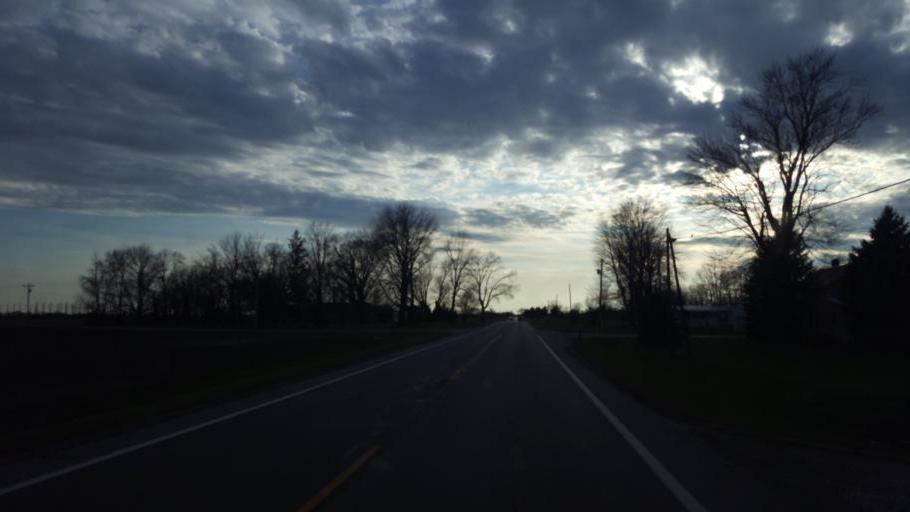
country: US
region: Ohio
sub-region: Marion County
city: Marion
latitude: 40.6298
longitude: -82.9901
